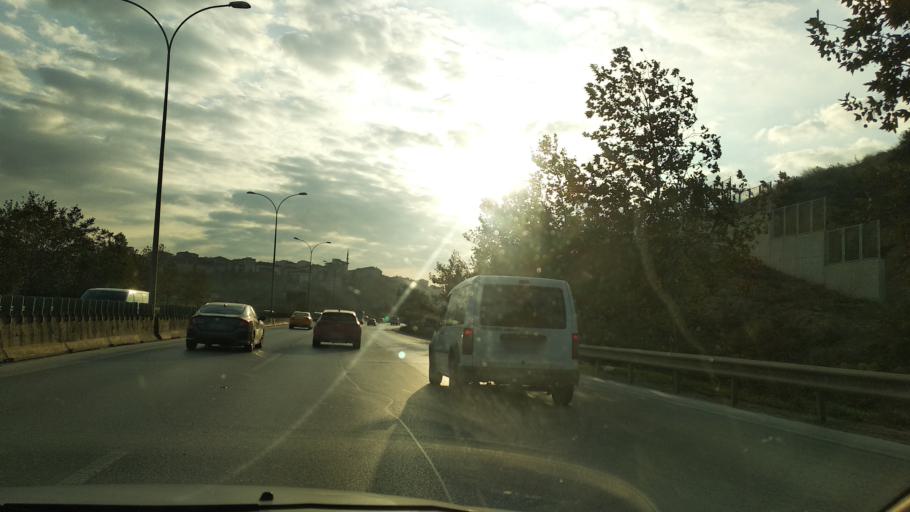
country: TR
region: Istanbul
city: Icmeler
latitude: 40.8762
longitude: 29.3029
